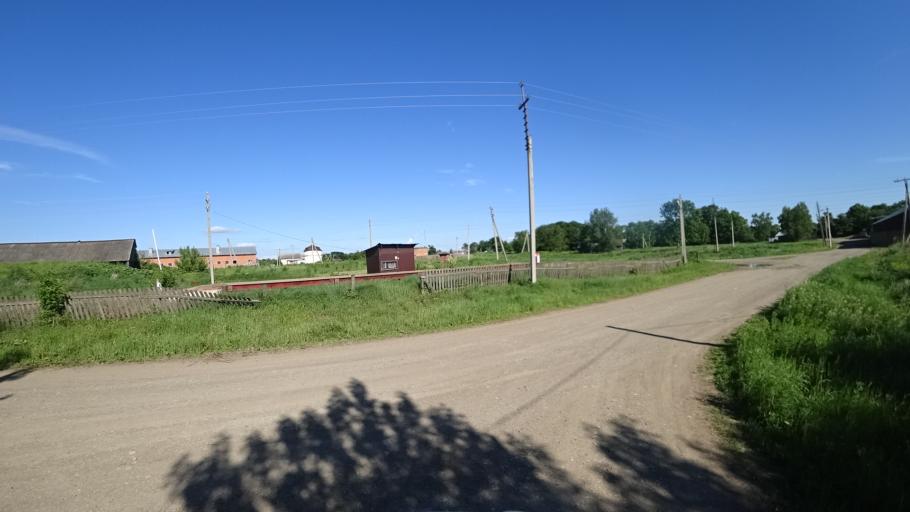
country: RU
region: Khabarovsk Krai
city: Khor
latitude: 47.8879
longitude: 134.9984
